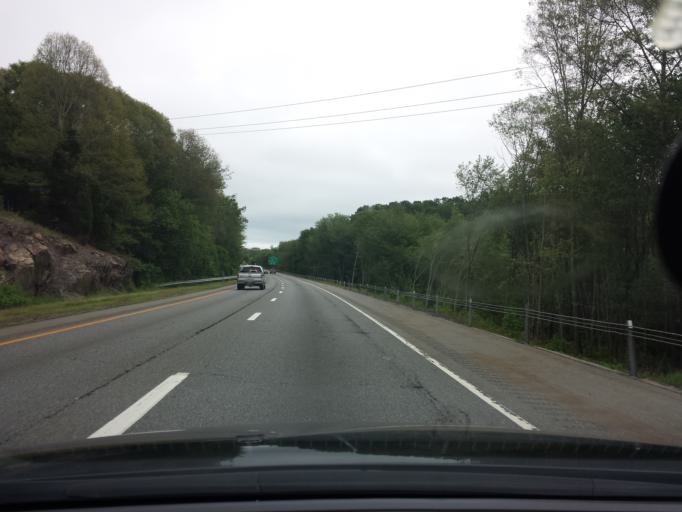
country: US
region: Connecticut
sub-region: New London County
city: Old Mystic
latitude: 41.3750
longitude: -71.9135
